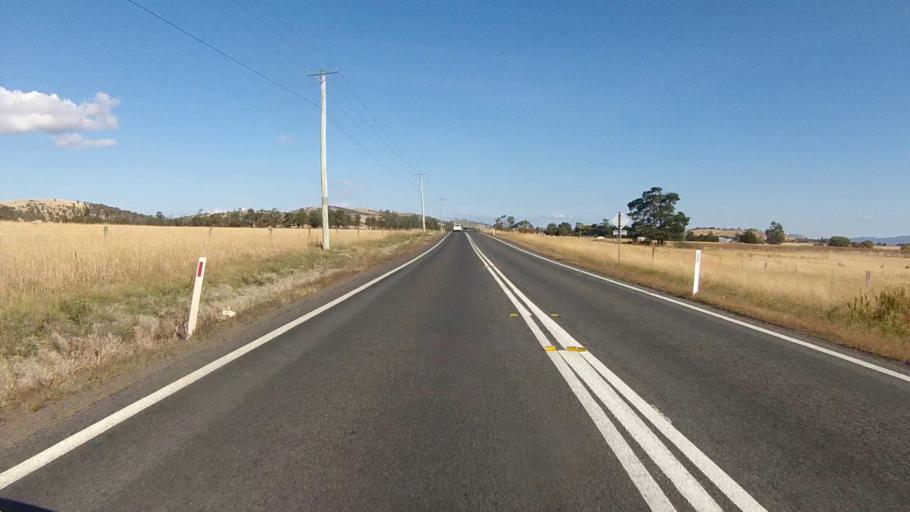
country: AU
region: Tasmania
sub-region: Sorell
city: Sorell
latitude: -42.7388
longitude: 147.5313
